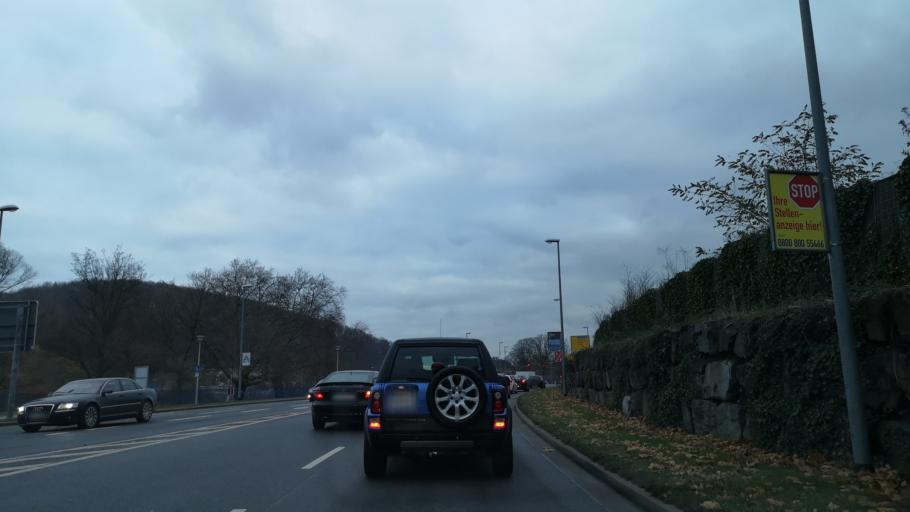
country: DE
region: North Rhine-Westphalia
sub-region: Regierungsbezirk Arnsberg
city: Hagen
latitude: 51.3549
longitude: 7.4524
